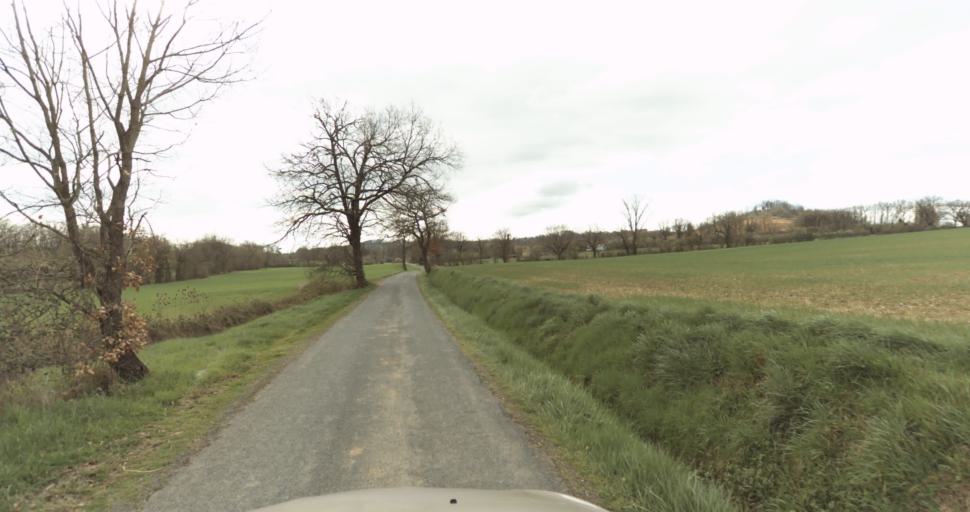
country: FR
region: Midi-Pyrenees
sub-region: Departement du Tarn
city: Puygouzon
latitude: 43.8841
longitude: 2.1950
